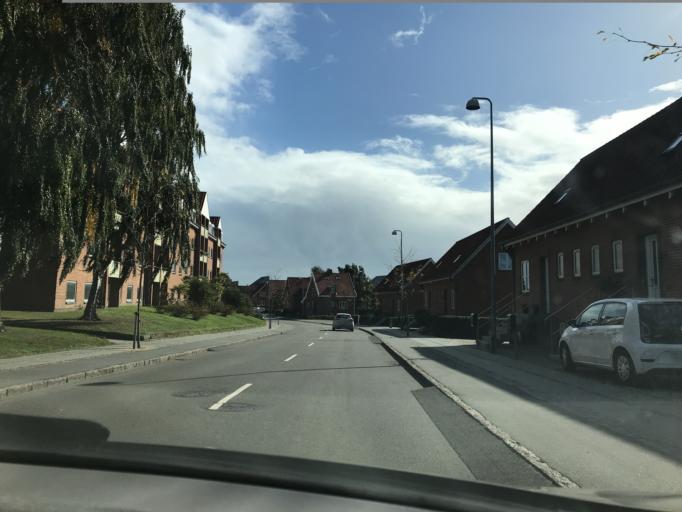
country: DK
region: Central Jutland
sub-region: Skanderborg Kommune
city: Skanderborg
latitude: 56.0350
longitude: 9.9217
